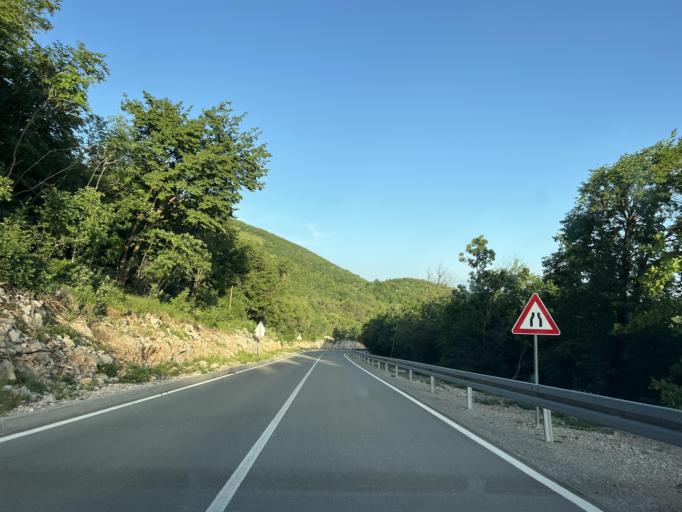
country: HR
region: Primorsko-Goranska
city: Skrljevo
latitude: 45.3919
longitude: 14.5585
